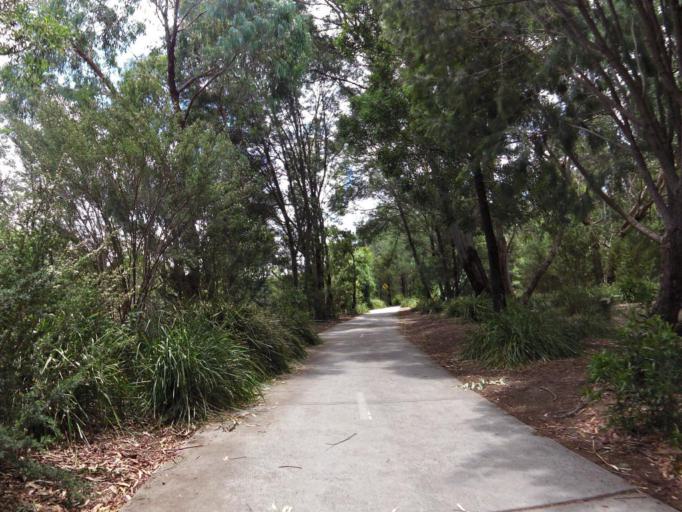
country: AU
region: Victoria
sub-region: Monash
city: Ashwood
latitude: -37.8635
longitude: 145.1011
